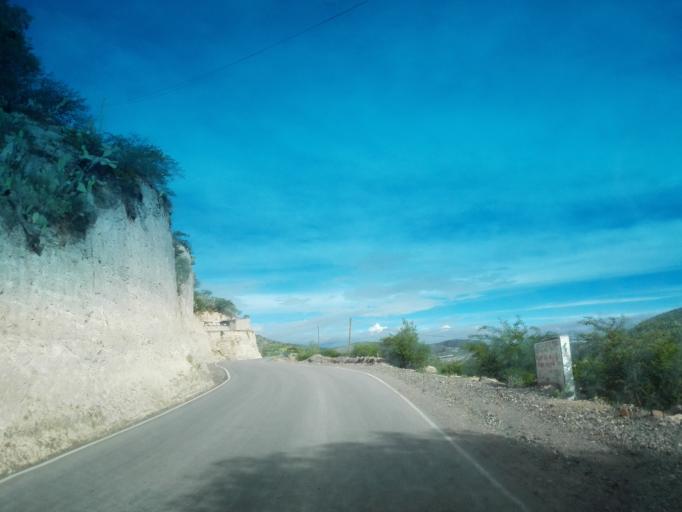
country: PE
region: Ayacucho
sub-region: Provincia de Huamanga
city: Pacaycasa
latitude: -13.0756
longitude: -74.2409
